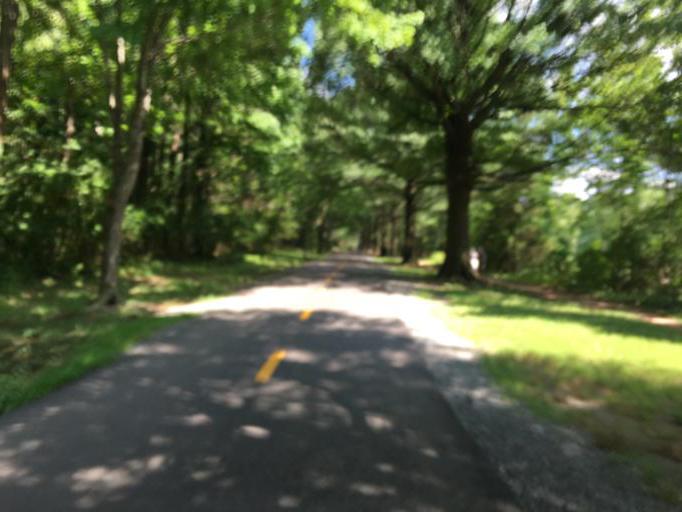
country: US
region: Virginia
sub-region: Fairfax County
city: Lincolnia
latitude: 38.8148
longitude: -77.1178
